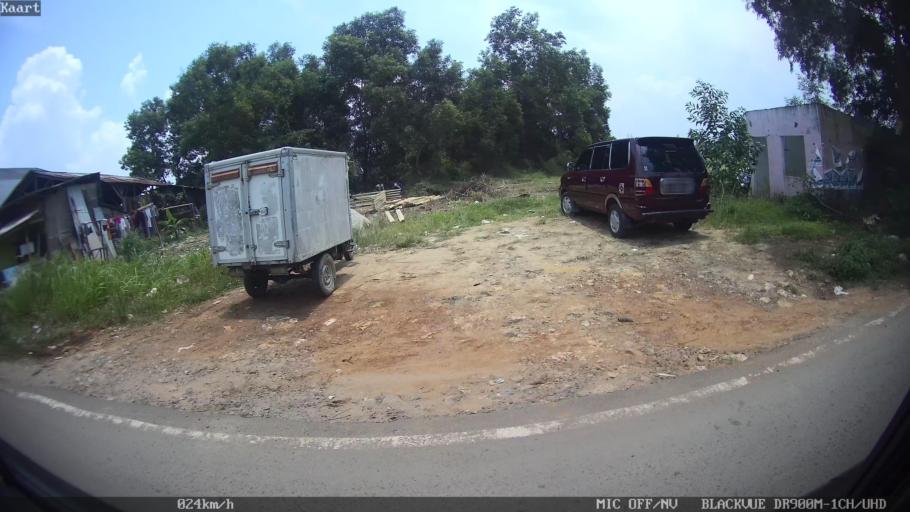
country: ID
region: Lampung
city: Kedaton
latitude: -5.3524
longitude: 105.2397
